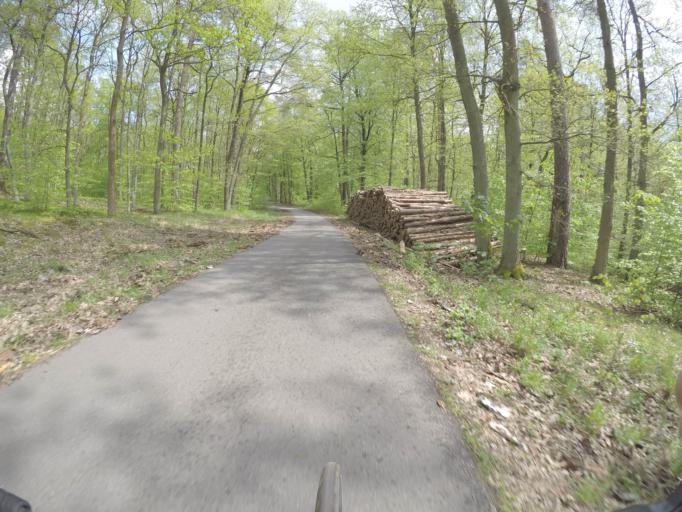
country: DE
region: Brandenburg
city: Joachimsthal
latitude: 52.9612
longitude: 13.7366
